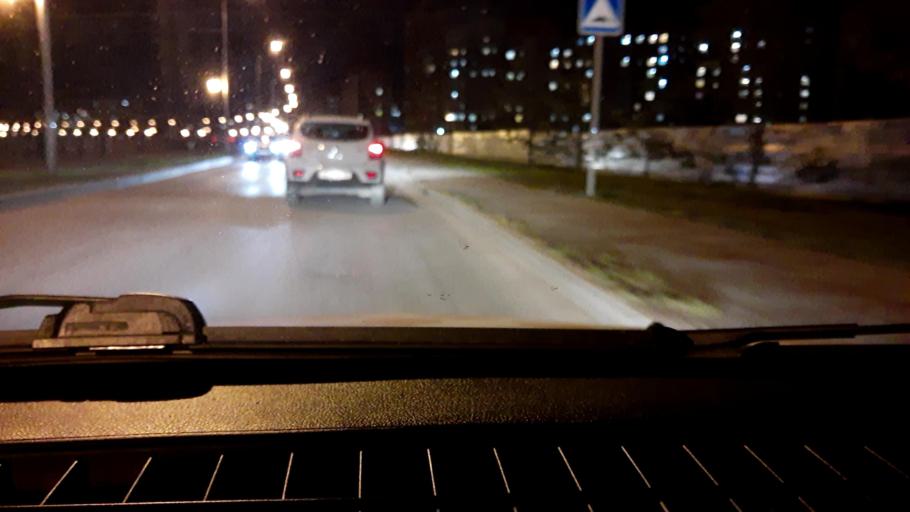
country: RU
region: Bashkortostan
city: Ufa
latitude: 54.7820
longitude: 56.0772
